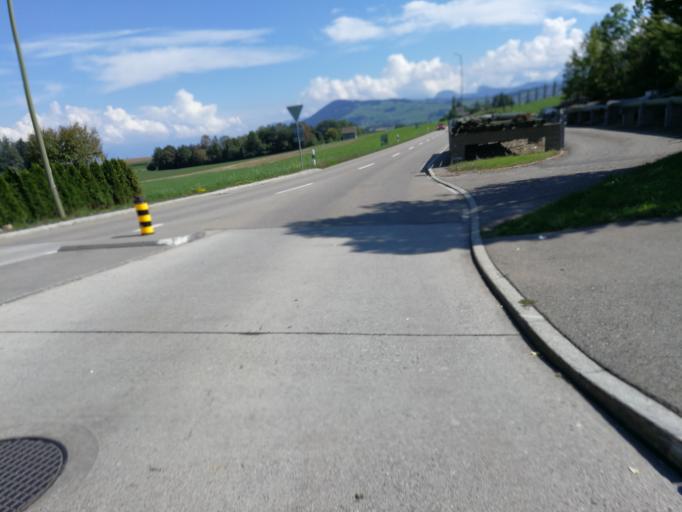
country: CH
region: Zurich
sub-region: Bezirk Horgen
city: Waedenswil / Eichweid
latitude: 47.2067
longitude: 8.6631
